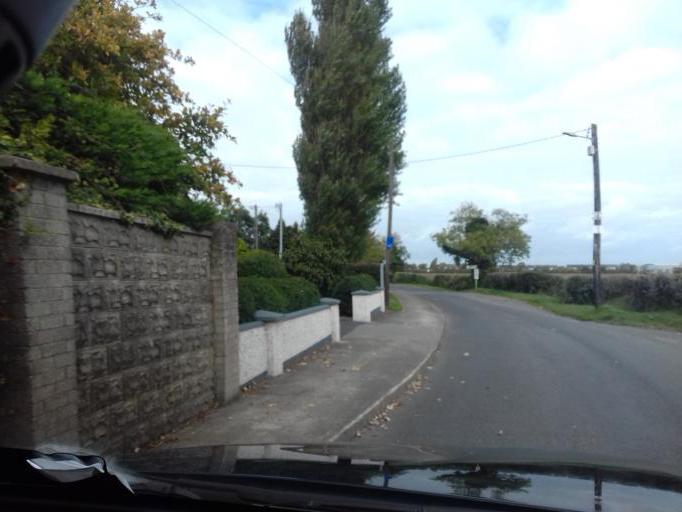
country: IE
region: Leinster
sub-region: Dublin City
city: Finglas
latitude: 53.4105
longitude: -6.2988
